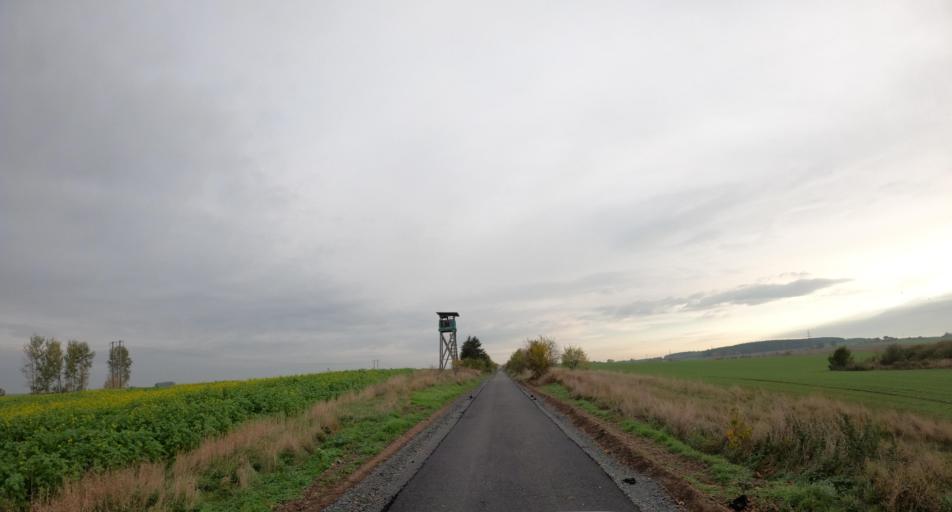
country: PL
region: West Pomeranian Voivodeship
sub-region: Powiat mysliborski
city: Nowogrodek Pomorski
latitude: 52.9815
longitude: 15.0445
